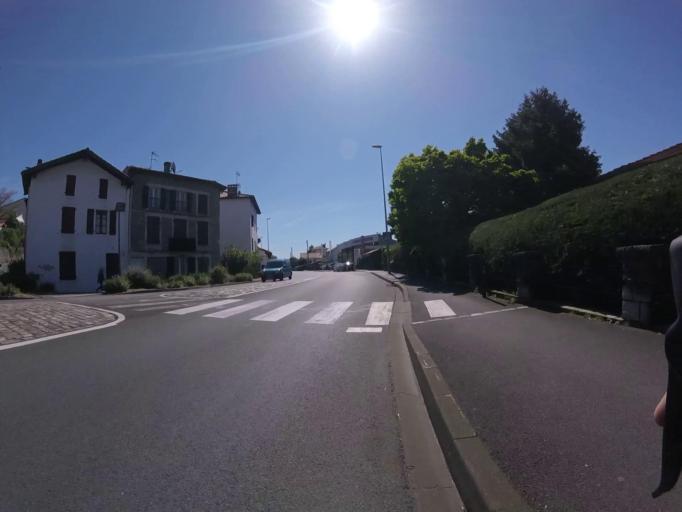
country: ES
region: Basque Country
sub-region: Provincia de Guipuzcoa
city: Irun
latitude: 43.3500
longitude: -1.7813
